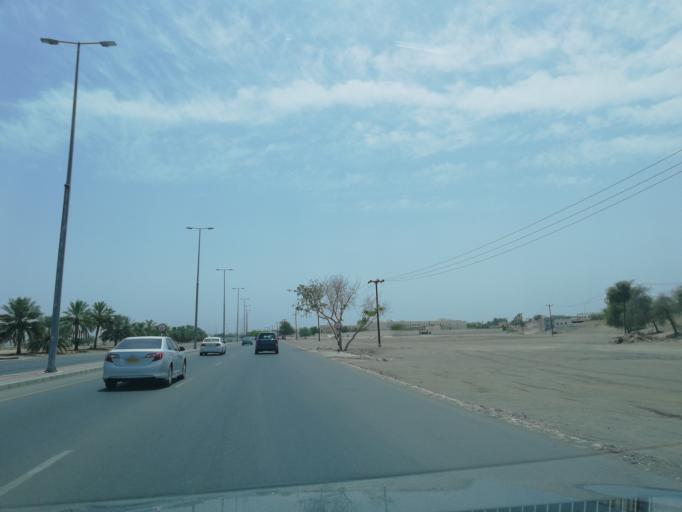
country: OM
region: Muhafazat Masqat
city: As Sib al Jadidah
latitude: 23.6746
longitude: 58.1655
